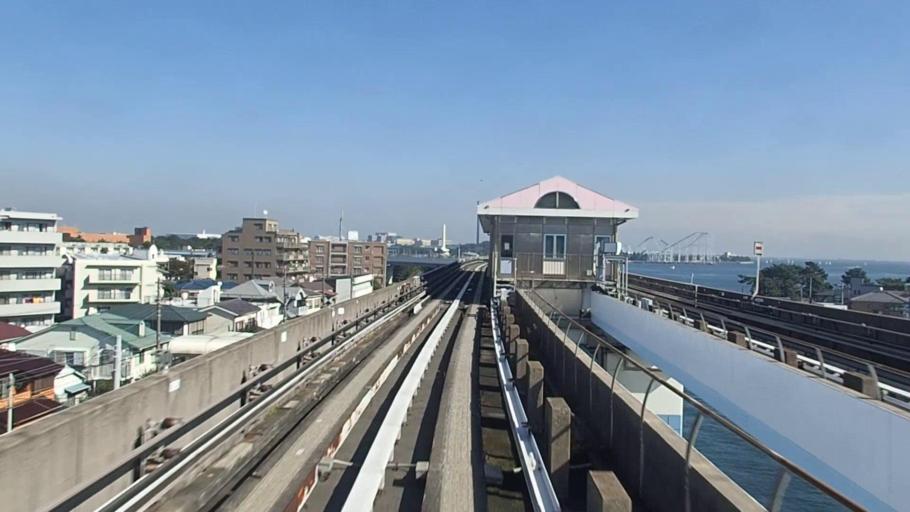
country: JP
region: Kanagawa
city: Yokosuka
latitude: 35.3304
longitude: 139.6311
